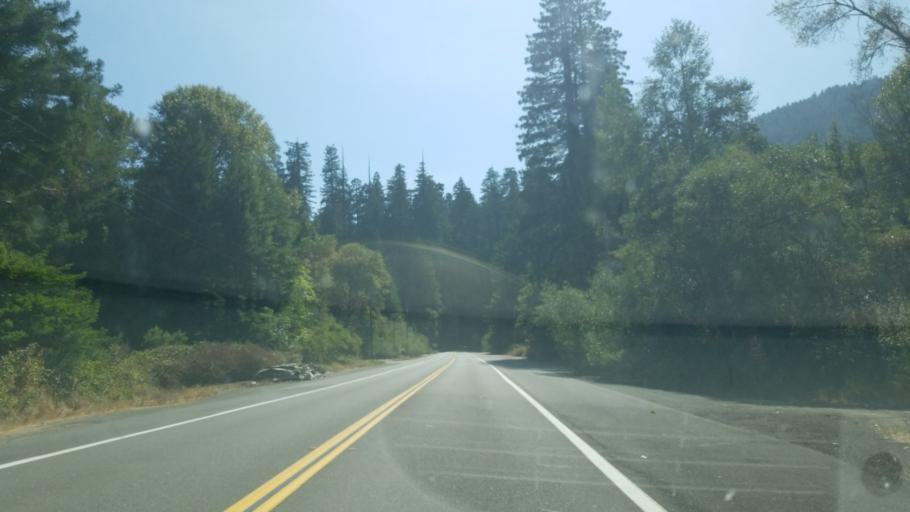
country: US
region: California
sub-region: Humboldt County
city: Redway
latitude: 40.3263
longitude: -123.9257
